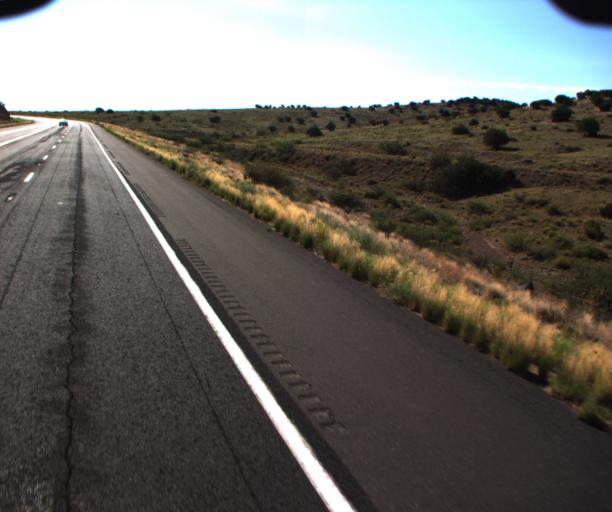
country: US
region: Arizona
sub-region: Greenlee County
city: Clifton
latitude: 32.8515
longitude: -109.3055
